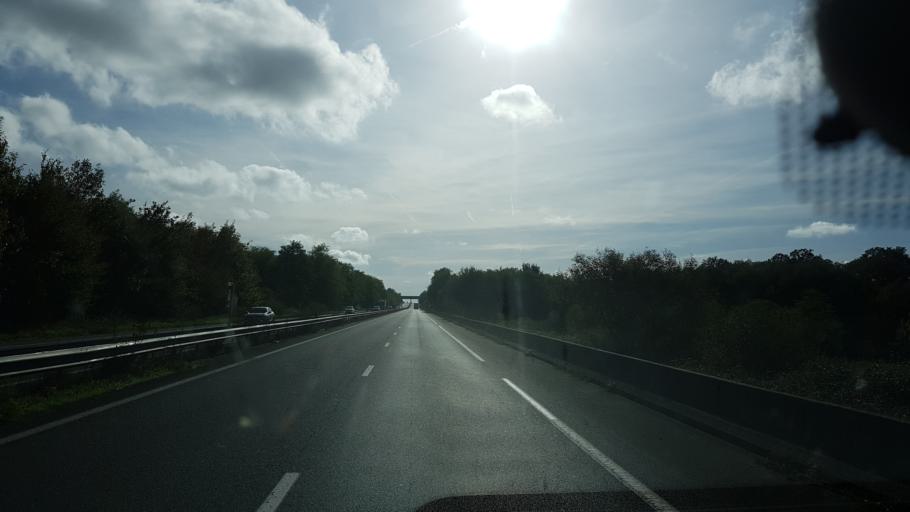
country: FR
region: Poitou-Charentes
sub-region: Departement de la Charente
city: Taponnat-Fleurignac
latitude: 45.7781
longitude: 0.4052
